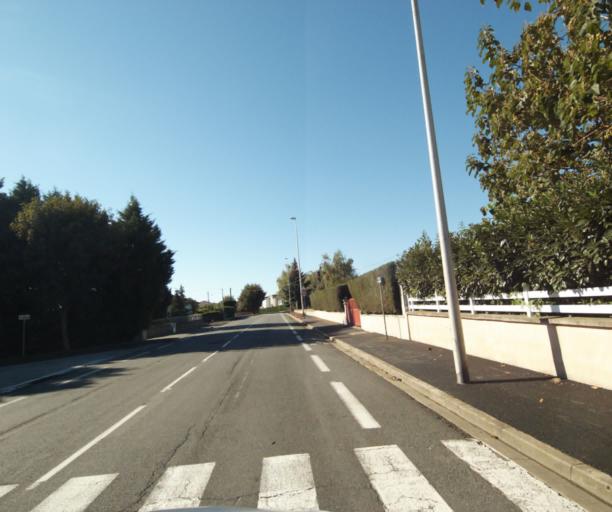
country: FR
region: Auvergne
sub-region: Departement du Puy-de-Dome
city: Gerzat
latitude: 45.8364
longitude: 3.1445
